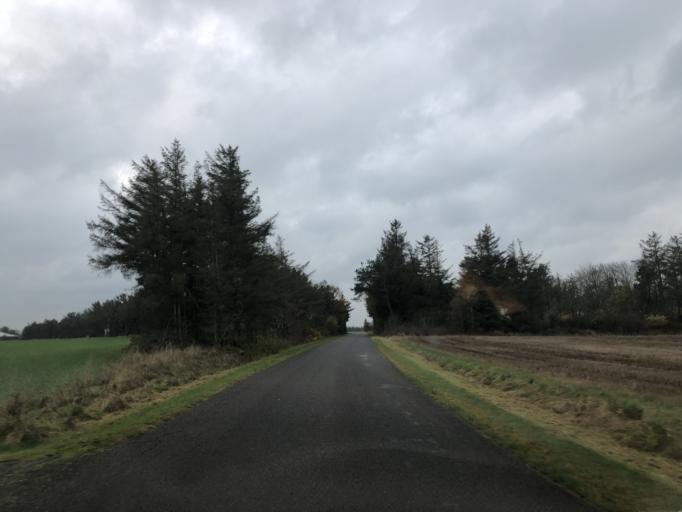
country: DK
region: Central Jutland
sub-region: Holstebro Kommune
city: Ulfborg
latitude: 56.3150
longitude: 8.2191
